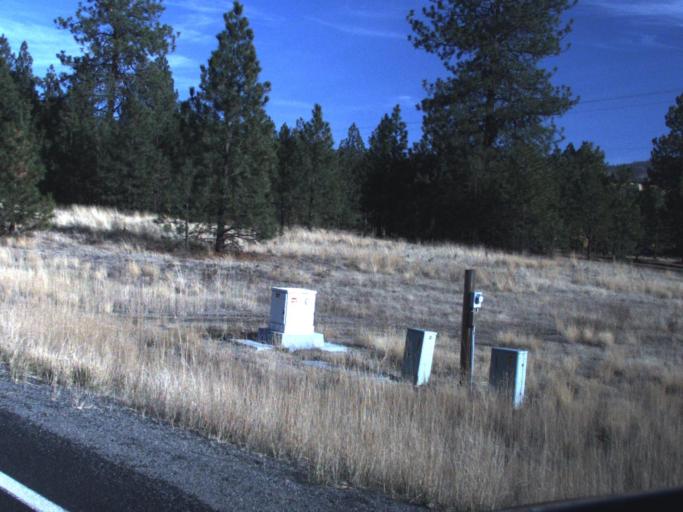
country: US
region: Washington
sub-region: Lincoln County
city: Davenport
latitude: 48.0163
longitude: -118.2389
